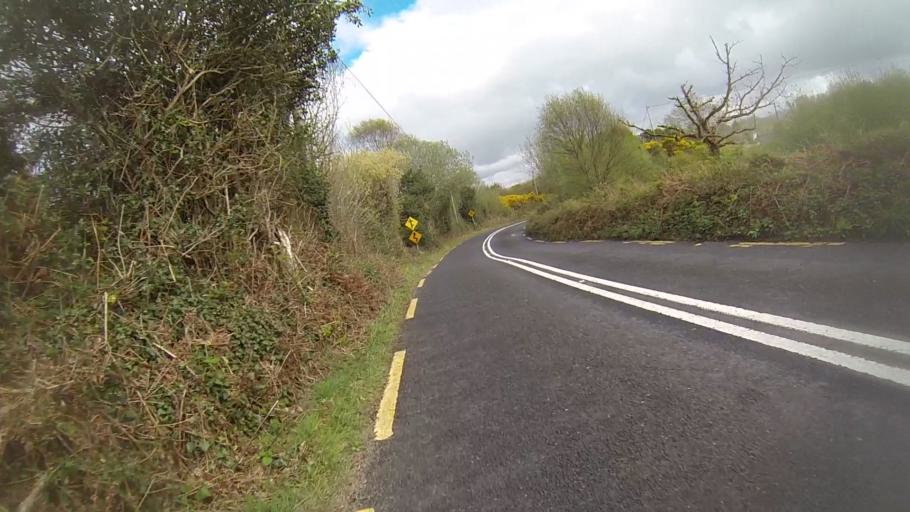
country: IE
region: Munster
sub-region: Ciarrai
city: Kenmare
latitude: 51.8313
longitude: -9.8253
